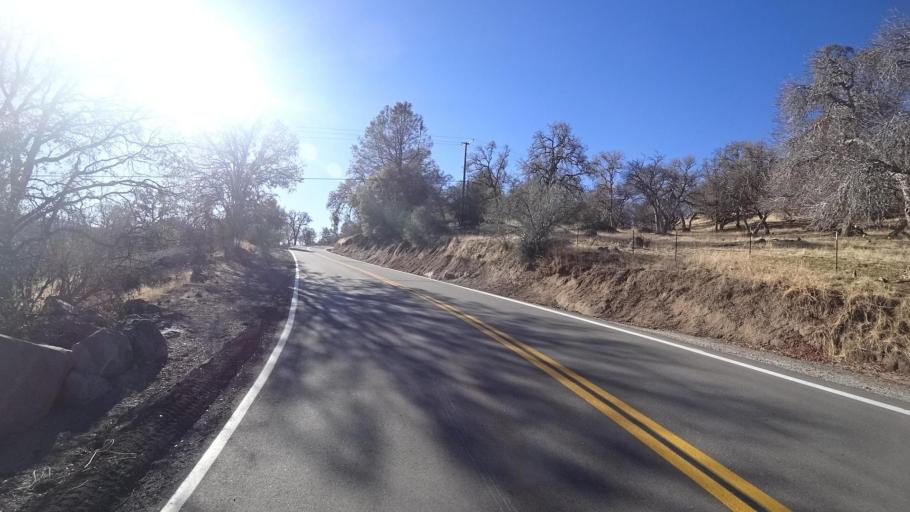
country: US
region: California
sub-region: Kern County
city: Alta Sierra
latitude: 35.7066
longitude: -118.7474
